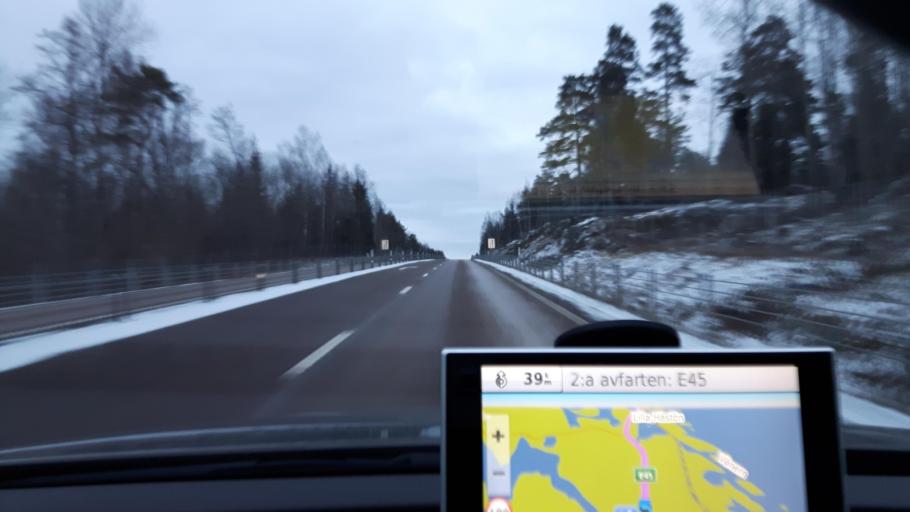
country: SE
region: Vaestra Goetaland
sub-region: Melleruds Kommun
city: Mellerud
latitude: 58.7433
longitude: 12.4785
